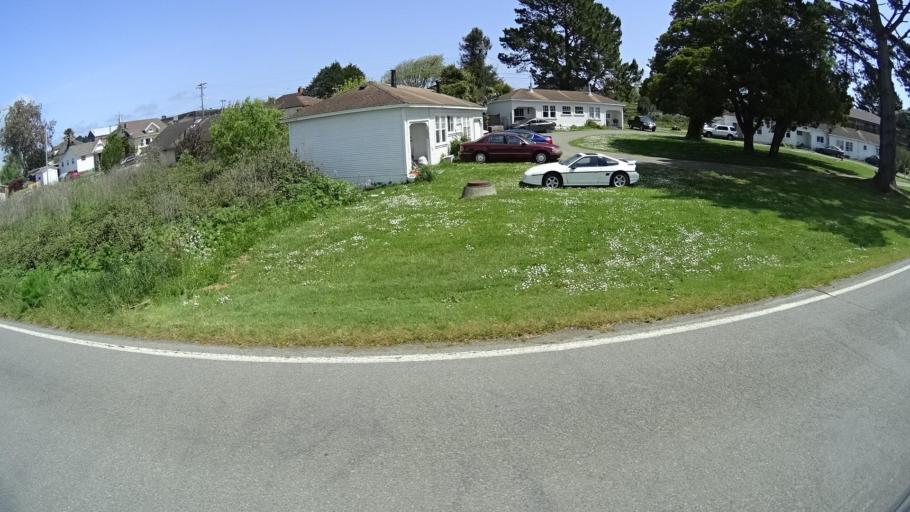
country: US
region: California
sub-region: Humboldt County
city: Ferndale
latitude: 40.6392
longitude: -124.2267
